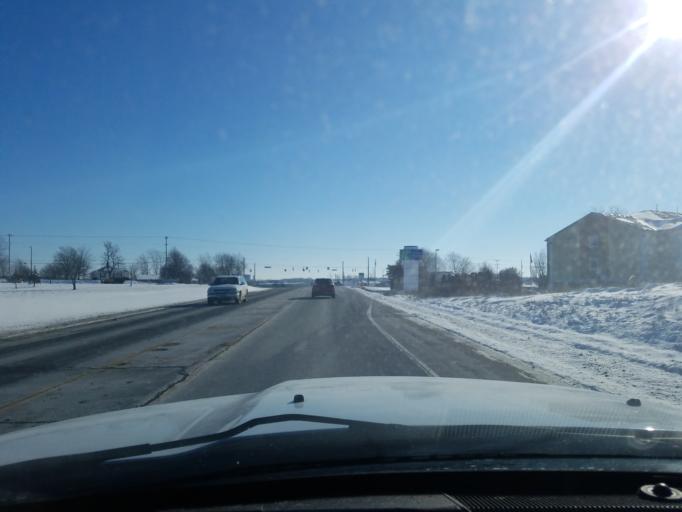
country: US
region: Indiana
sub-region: Noble County
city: Kendallville
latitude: 41.4462
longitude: -85.2335
